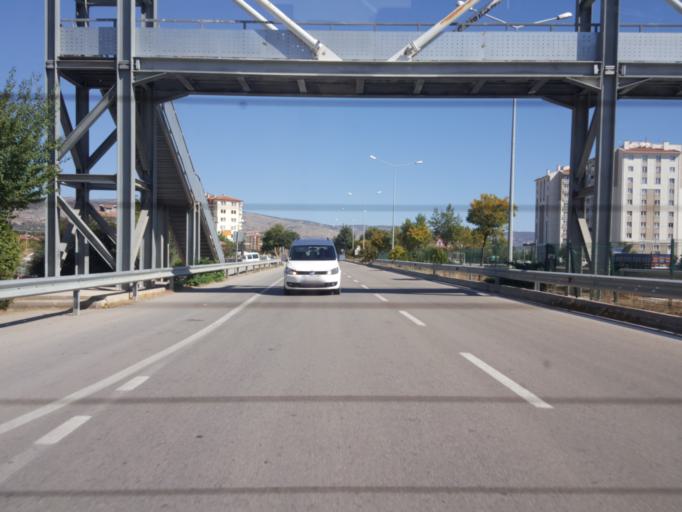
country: TR
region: Tokat
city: Zile
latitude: 40.2997
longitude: 35.8954
